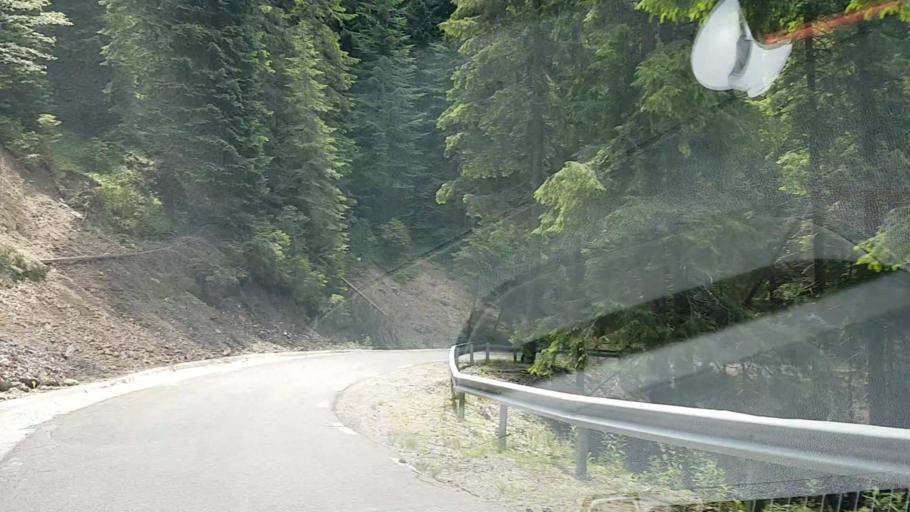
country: RO
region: Suceava
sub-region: Municipiul Campulung Moldovenesc
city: Campulung Moldovenesc
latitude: 47.4452
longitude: 25.5563
